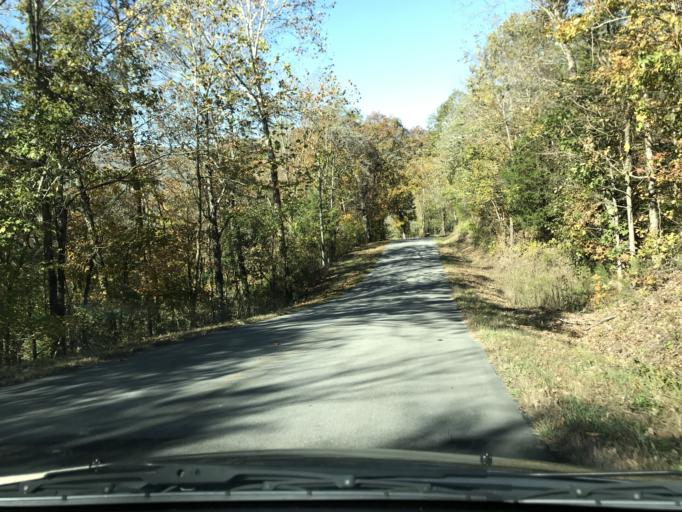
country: US
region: Georgia
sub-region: Dade County
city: Trenton
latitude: 34.9083
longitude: -85.4705
